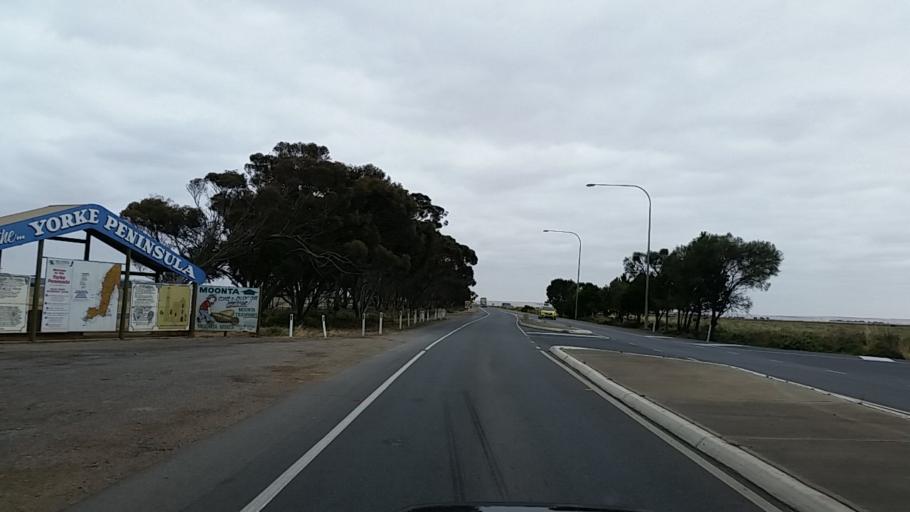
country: AU
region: South Australia
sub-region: Wakefield
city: Balaklava
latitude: -34.1802
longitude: 138.1539
